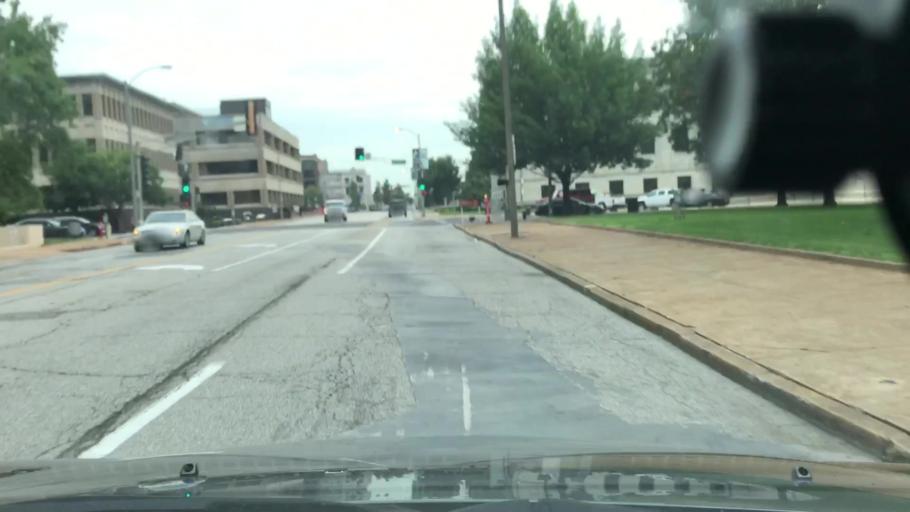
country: US
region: Missouri
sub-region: City of Saint Louis
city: St. Louis
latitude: 38.6297
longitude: -90.2004
